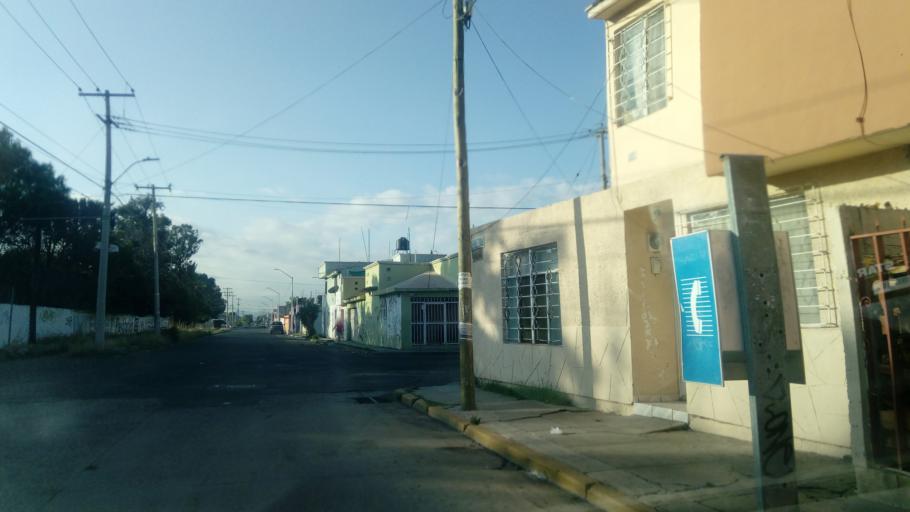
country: MX
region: Durango
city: Victoria de Durango
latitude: 24.0488
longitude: -104.6167
